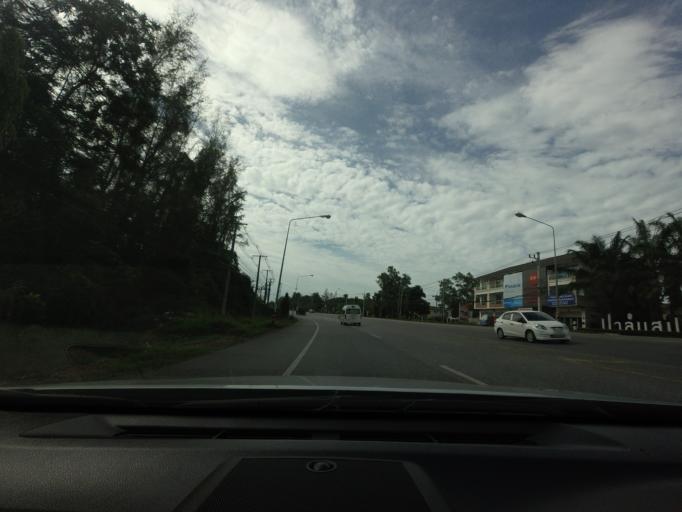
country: TH
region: Songkhla
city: Hat Yai
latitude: 6.9706
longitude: 100.4295
